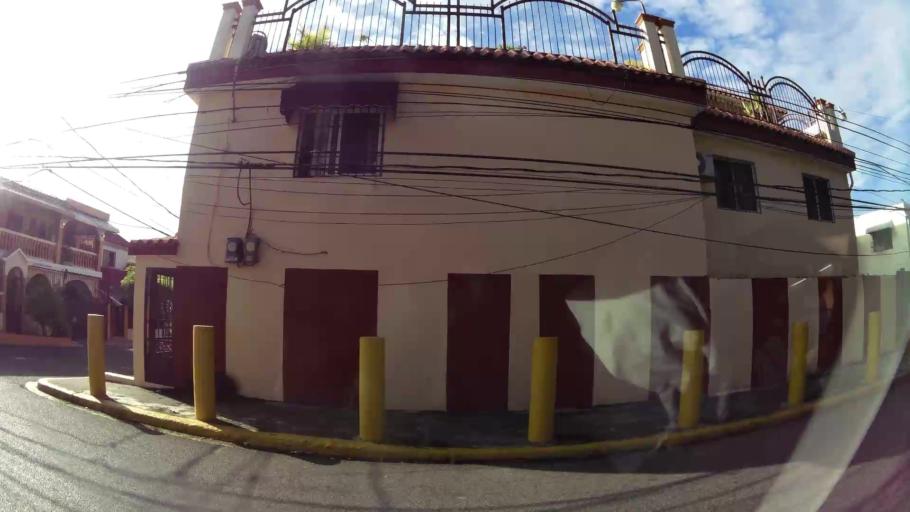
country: DO
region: Santo Domingo
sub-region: Santo Domingo
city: Santo Domingo Este
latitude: 18.4868
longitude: -69.8593
